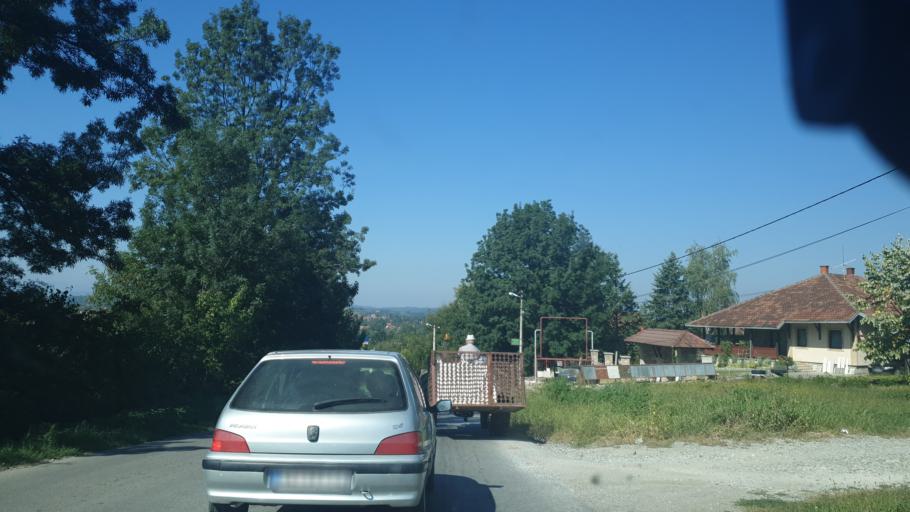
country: RS
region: Central Serbia
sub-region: Kolubarski Okrug
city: Mionica
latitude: 44.2556
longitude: 20.0988
